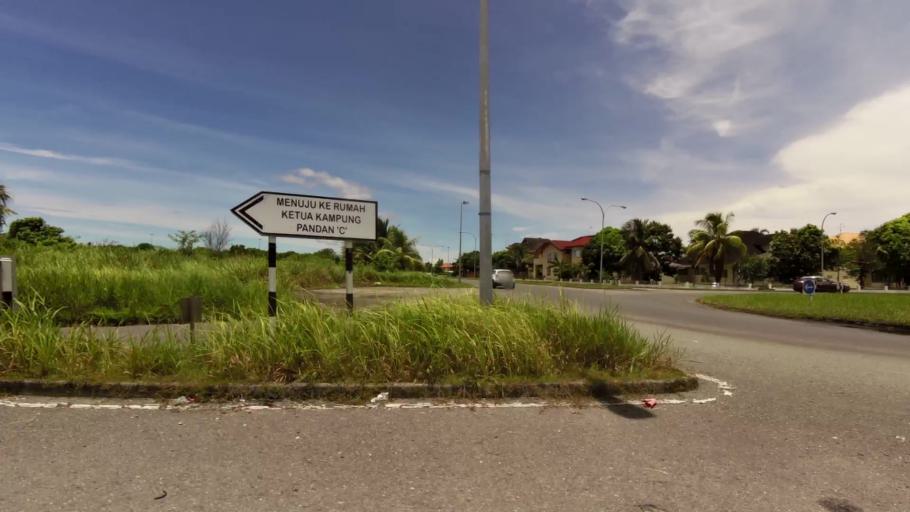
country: BN
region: Belait
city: Kuala Belait
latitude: 4.5837
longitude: 114.2322
